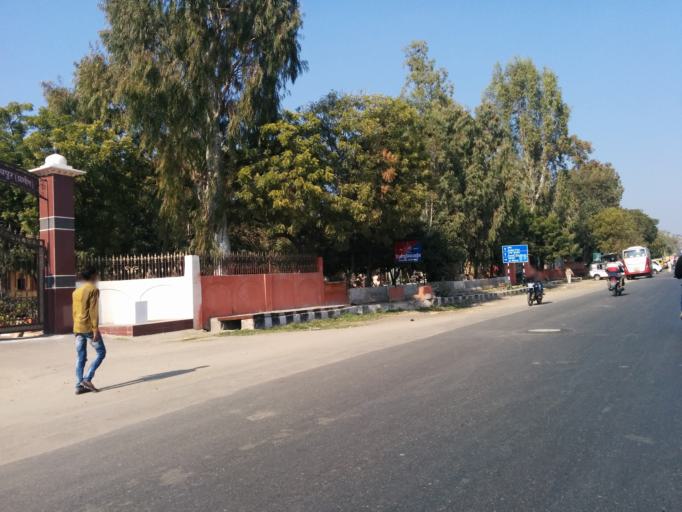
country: IN
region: Rajasthan
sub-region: Jaipur
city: Jaipur
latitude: 26.9511
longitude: 75.8414
